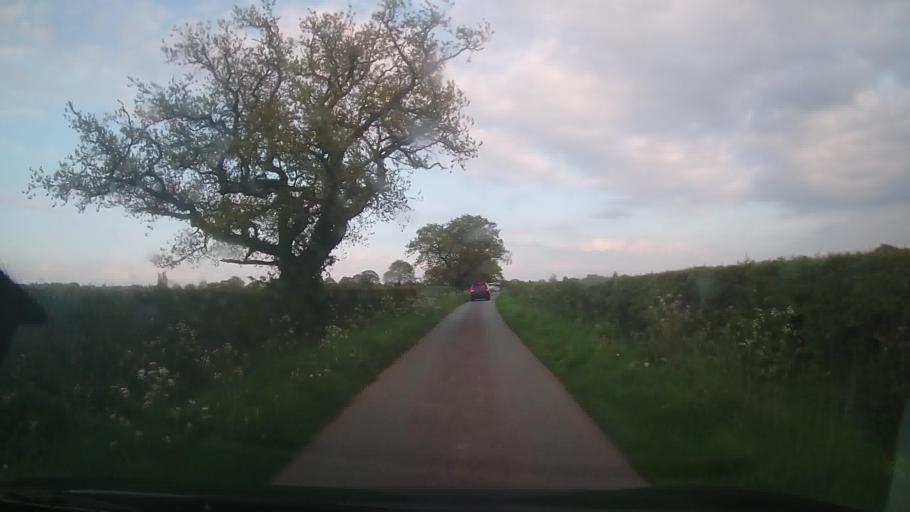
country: GB
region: England
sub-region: Shropshire
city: Ellesmere
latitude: 52.9312
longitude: -2.8405
